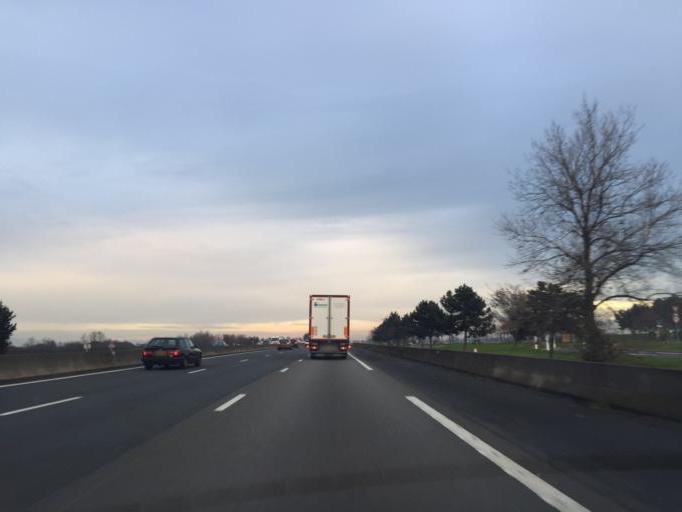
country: FR
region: Rhone-Alpes
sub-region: Departement de l'Ain
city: Guereins
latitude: 46.1359
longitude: 4.7663
